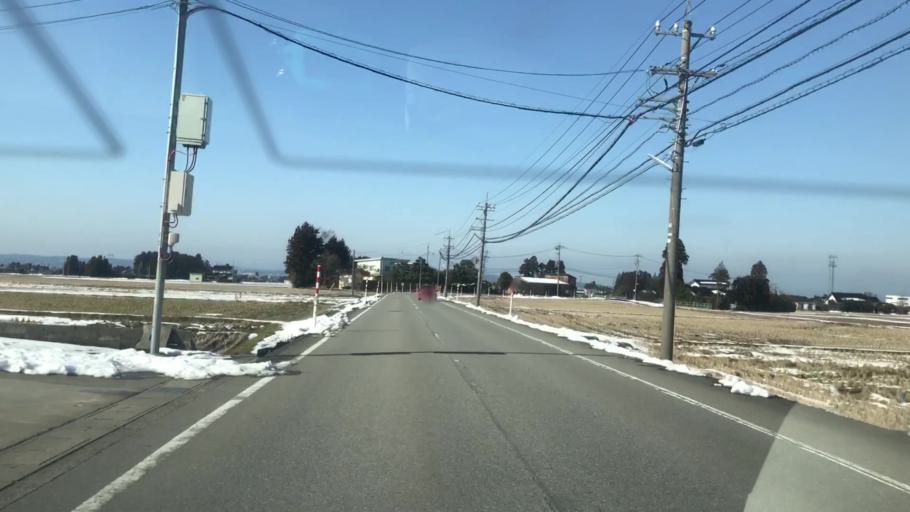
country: JP
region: Toyama
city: Toyama-shi
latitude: 36.6283
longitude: 137.2736
